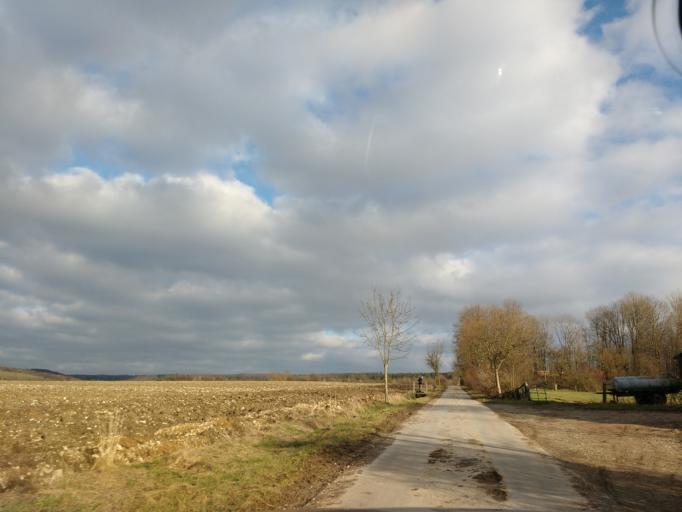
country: DE
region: North Rhine-Westphalia
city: Bad Lippspringe
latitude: 51.7749
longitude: 8.8497
